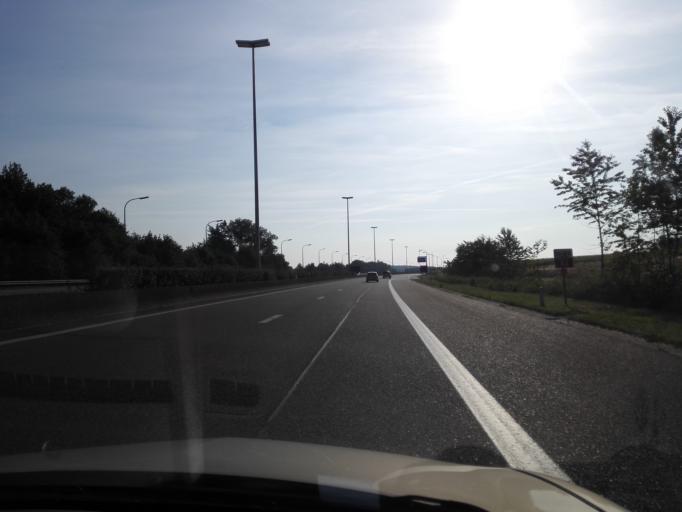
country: BE
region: Flanders
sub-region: Provincie Vlaams-Brabant
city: Aarschot
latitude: 50.9636
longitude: 4.8258
